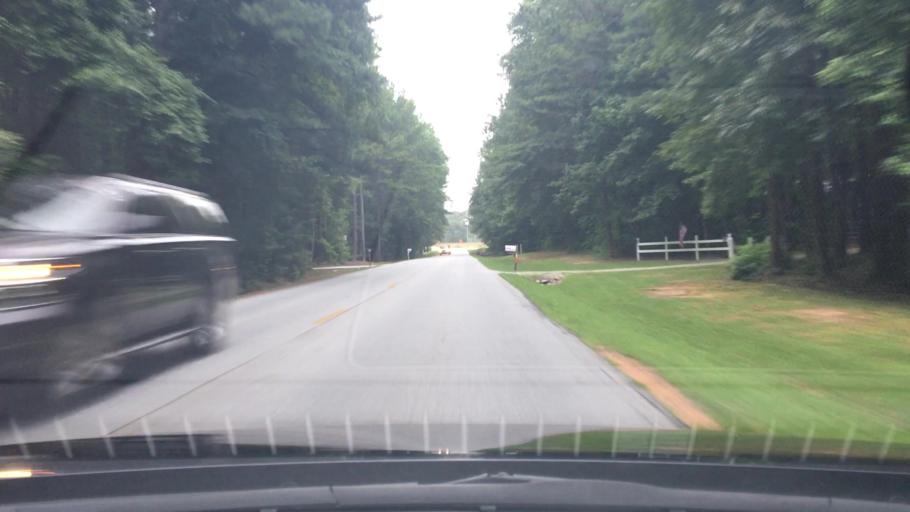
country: US
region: Georgia
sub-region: Coweta County
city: Senoia
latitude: 33.3079
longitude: -84.4694
